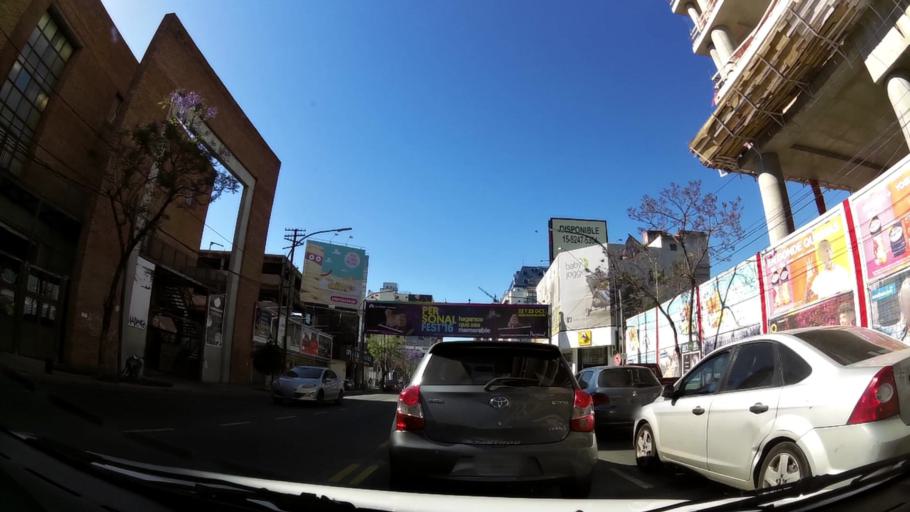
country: AR
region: Buenos Aires
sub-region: Partido de Vicente Lopez
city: Olivos
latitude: -34.5248
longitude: -58.4724
